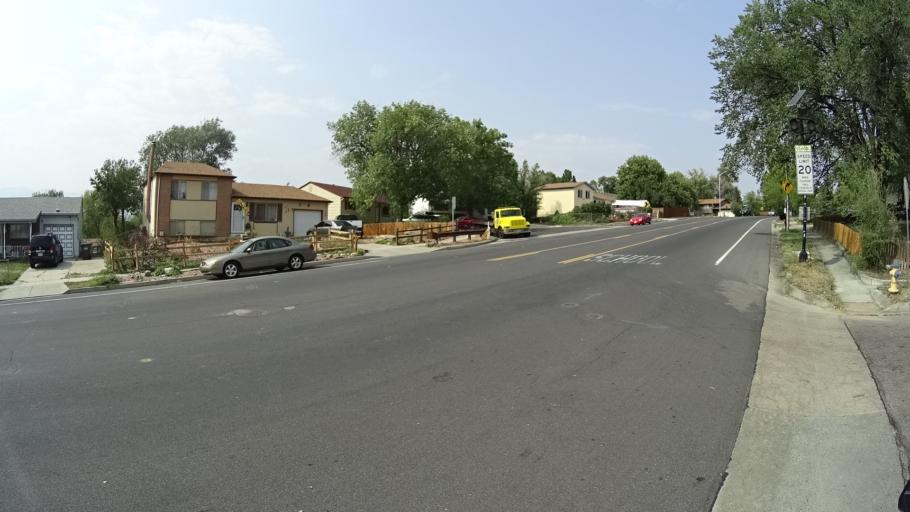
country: US
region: Colorado
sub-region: El Paso County
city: Cimarron Hills
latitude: 38.8304
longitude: -104.7485
